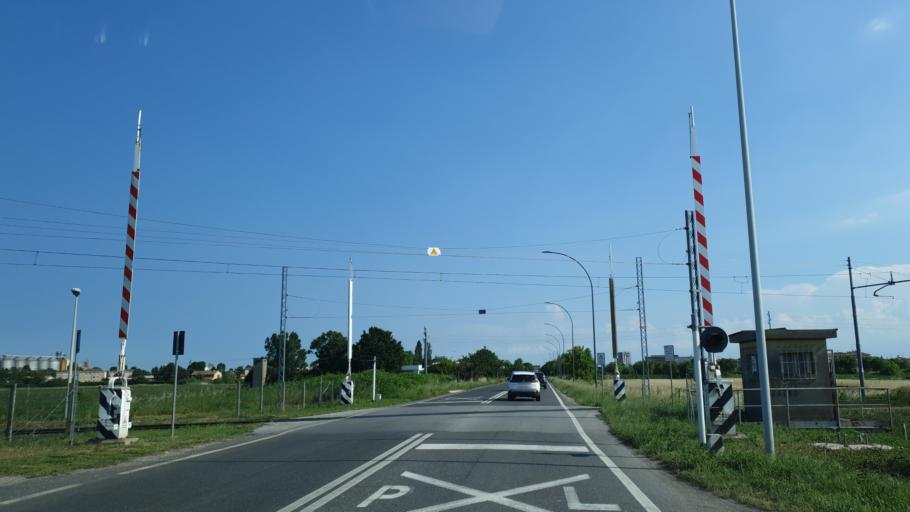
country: IT
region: Emilia-Romagna
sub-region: Provincia di Ravenna
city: Ravenna
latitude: 44.4345
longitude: 12.2131
